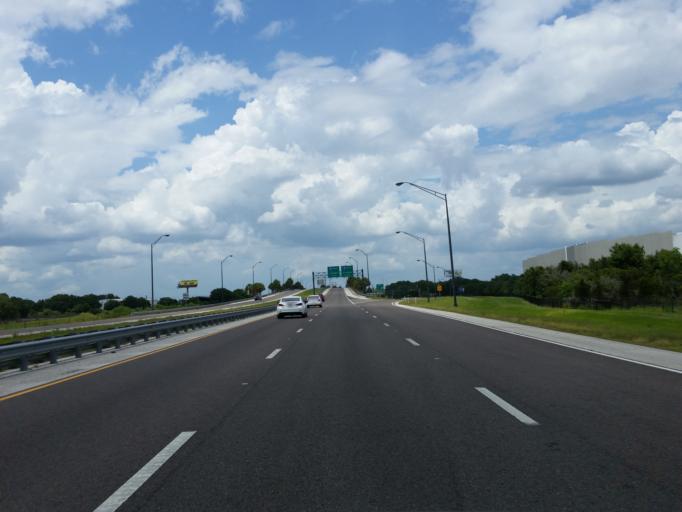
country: US
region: Florida
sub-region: Polk County
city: Winston
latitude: 28.0243
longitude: -82.0400
